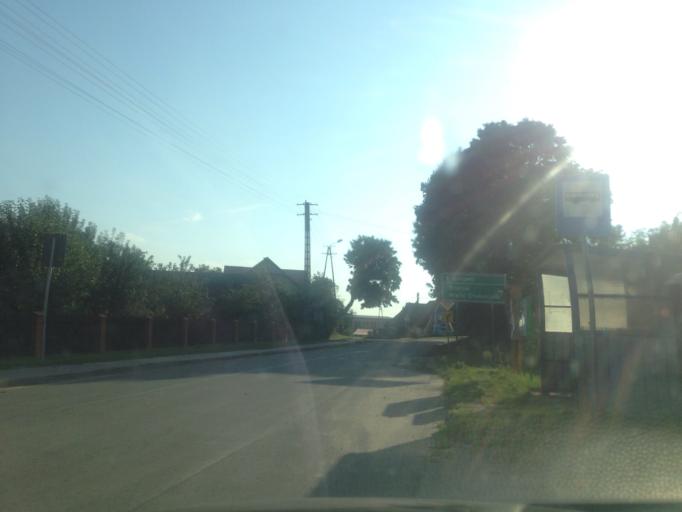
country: PL
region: Kujawsko-Pomorskie
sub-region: Powiat brodnicki
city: Brzozie
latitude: 53.2903
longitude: 19.6920
